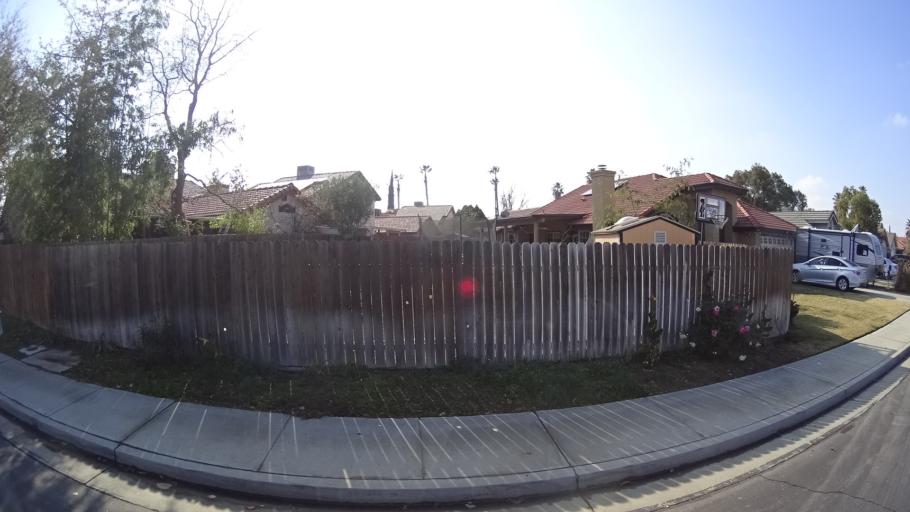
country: US
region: California
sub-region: Kern County
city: Greenacres
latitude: 35.3069
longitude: -119.0897
